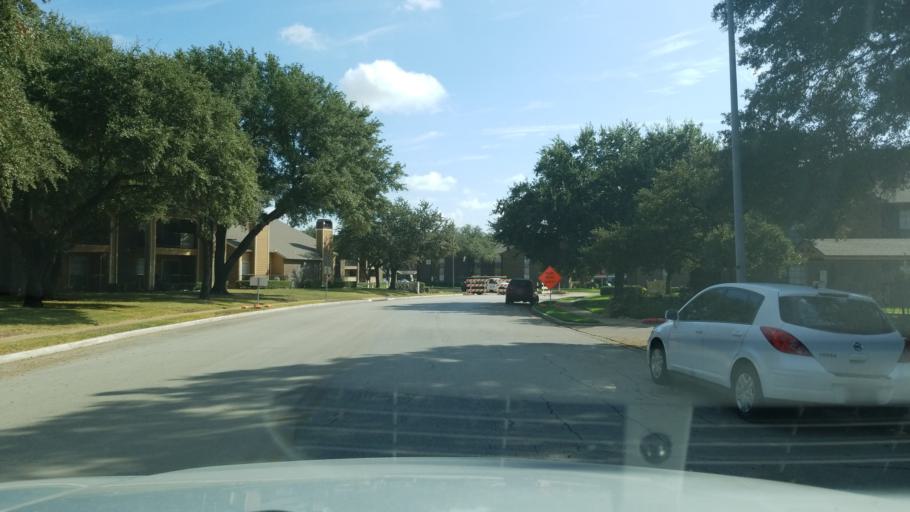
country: US
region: Texas
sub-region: Tarrant County
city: Euless
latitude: 32.8487
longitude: -97.0736
